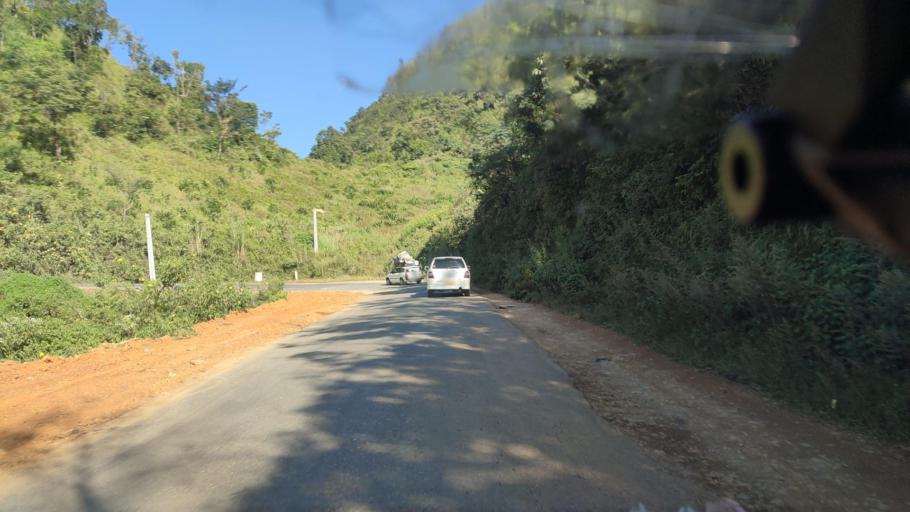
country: MM
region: Shan
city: Taunggyi
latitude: 20.8768
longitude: 97.5113
